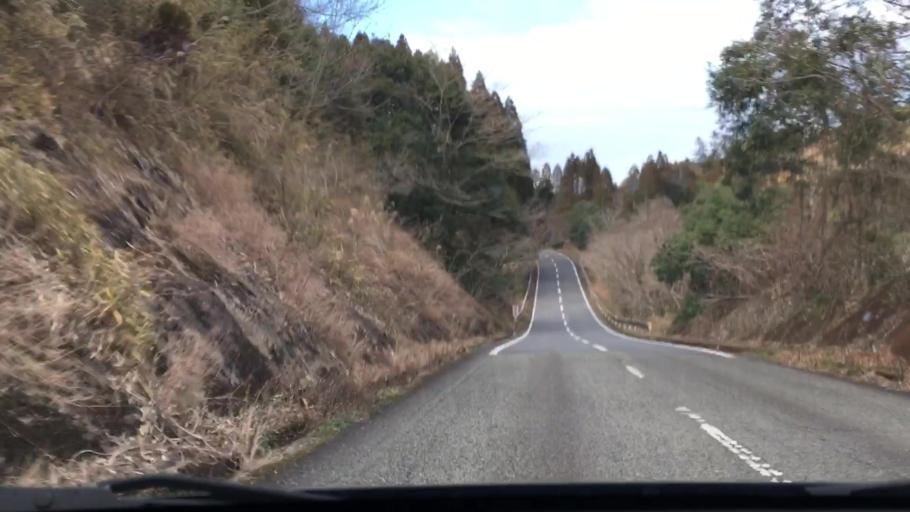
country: JP
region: Miyazaki
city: Nichinan
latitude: 31.7099
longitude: 131.3266
